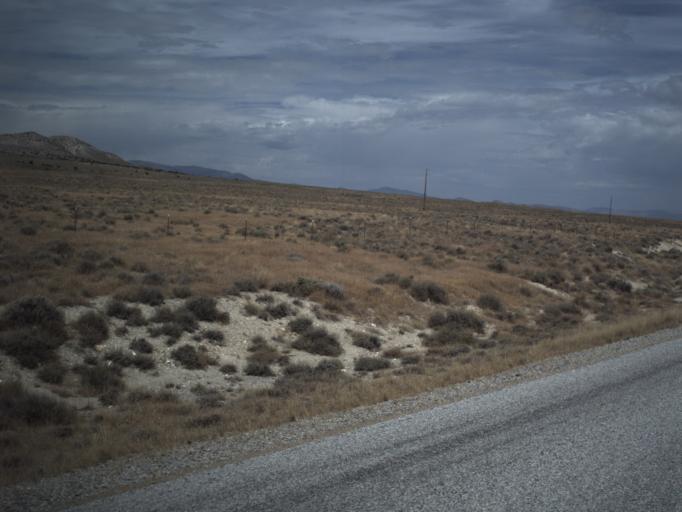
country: US
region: Utah
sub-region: Tooele County
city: Wendover
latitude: 41.5058
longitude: -113.6027
